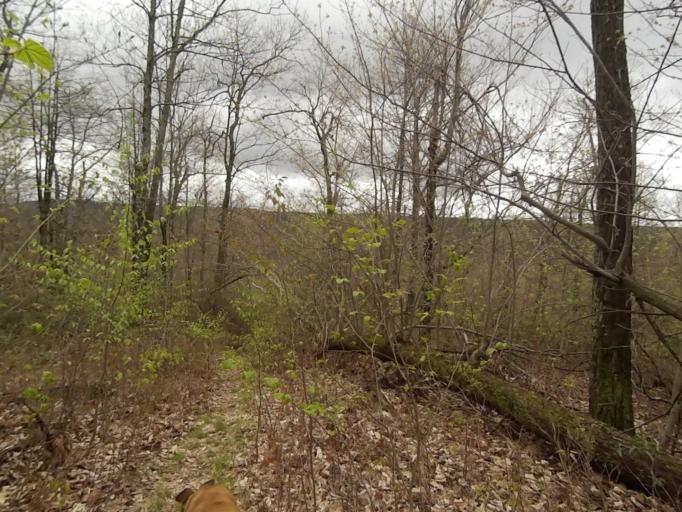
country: US
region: Pennsylvania
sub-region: Centre County
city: Boalsburg
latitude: 40.7476
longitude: -77.7532
